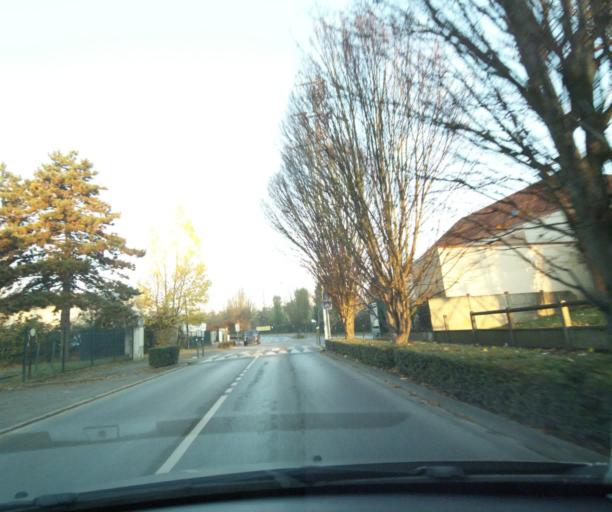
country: FR
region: Ile-de-France
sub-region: Departement de Seine-Saint-Denis
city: Gagny
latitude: 48.8732
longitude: 2.5323
